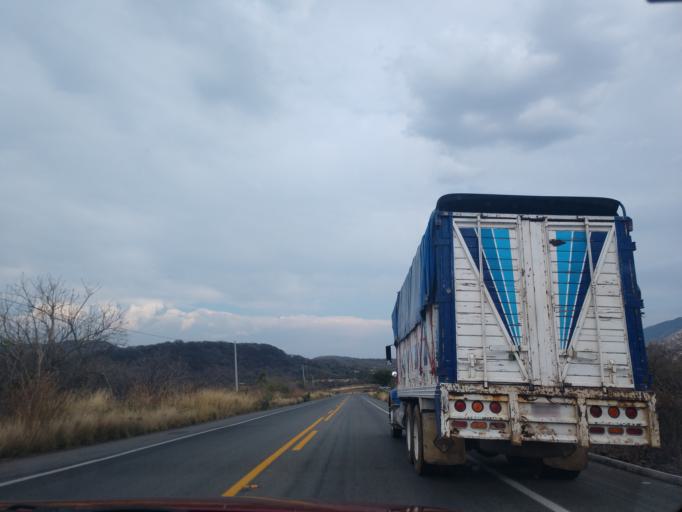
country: MX
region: Jalisco
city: La Manzanilla de la Paz
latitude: 20.1213
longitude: -103.1578
